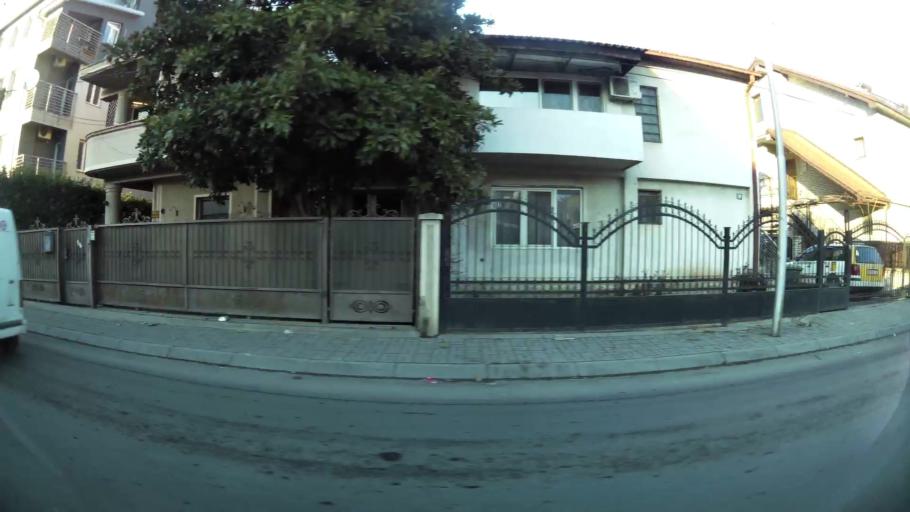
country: MK
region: Karpos
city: Skopje
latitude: 41.9937
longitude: 21.4035
